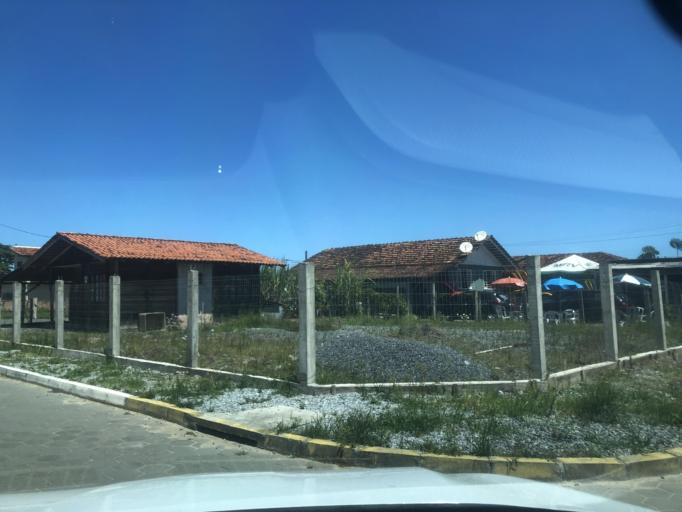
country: BR
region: Santa Catarina
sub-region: Sao Francisco Do Sul
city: Sao Francisco do Sul
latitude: -26.2348
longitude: -48.5215
